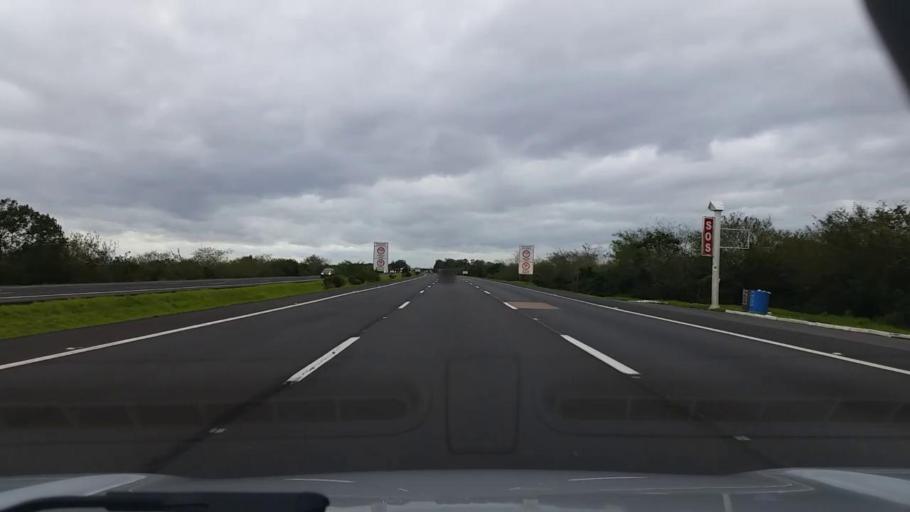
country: BR
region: Rio Grande do Sul
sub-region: Rolante
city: Rolante
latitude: -29.8839
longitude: -50.5653
